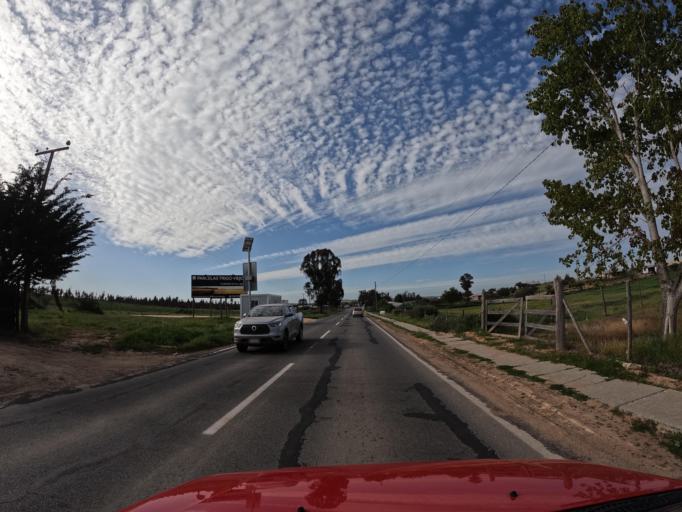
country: CL
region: O'Higgins
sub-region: Provincia de Colchagua
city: Santa Cruz
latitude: -34.2515
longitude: -71.7278
